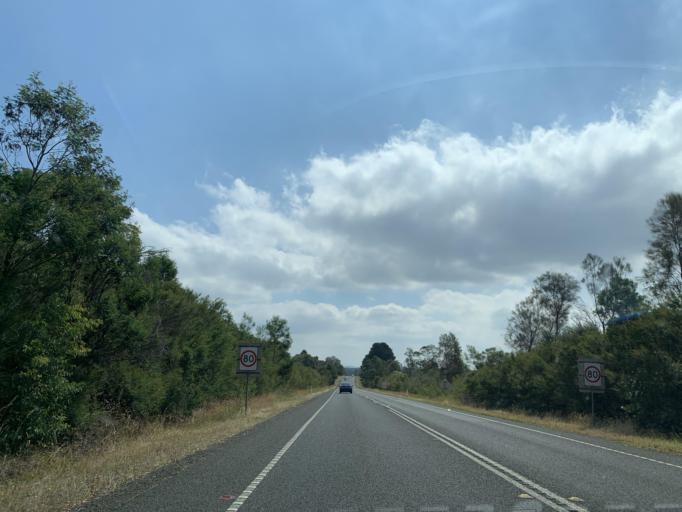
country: AU
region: Victoria
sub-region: Latrobe
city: Traralgon
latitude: -38.2012
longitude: 146.4769
